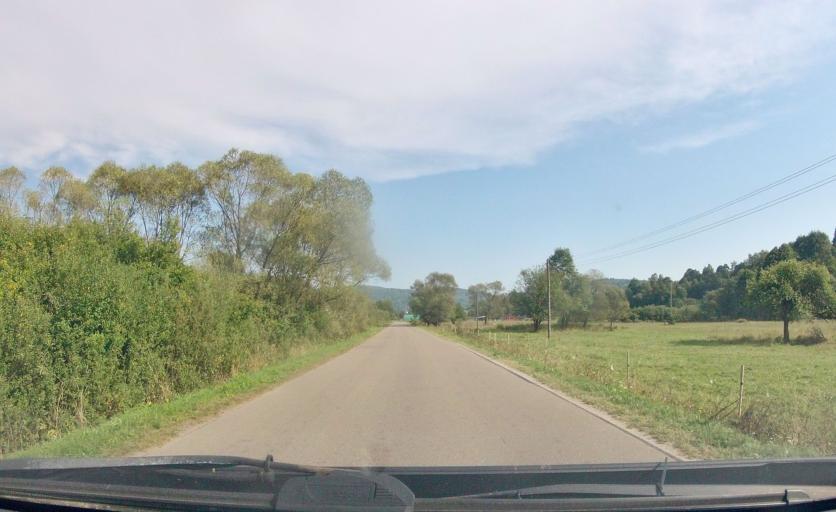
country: PL
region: Subcarpathian Voivodeship
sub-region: Powiat jasielski
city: Krempna
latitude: 49.5006
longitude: 21.5446
